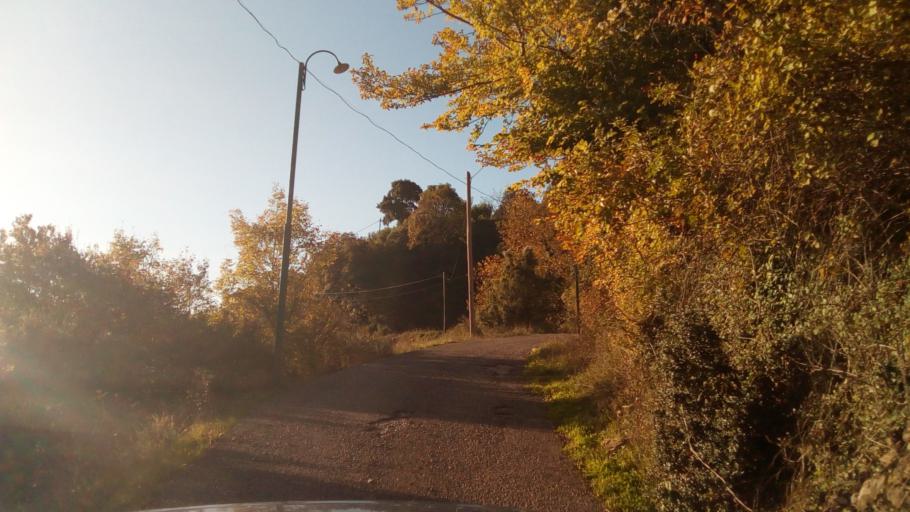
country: GR
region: West Greece
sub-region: Nomos Aitolias kai Akarnanias
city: Thermo
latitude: 38.5932
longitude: 21.7978
